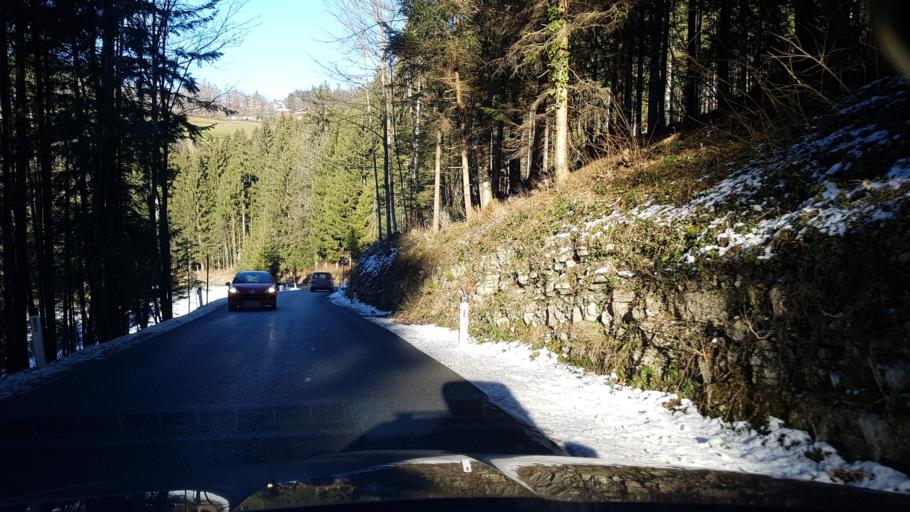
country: AT
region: Salzburg
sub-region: Politischer Bezirk Hallein
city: Golling an der Salzach
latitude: 47.6237
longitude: 13.1884
